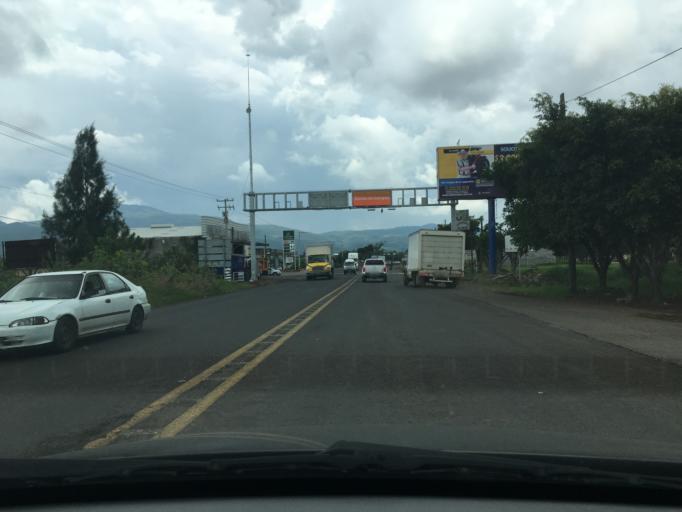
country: MX
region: Michoacan
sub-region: Los Reyes
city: La Higuerita (Colonia San Rafael)
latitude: 19.6198
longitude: -102.4860
